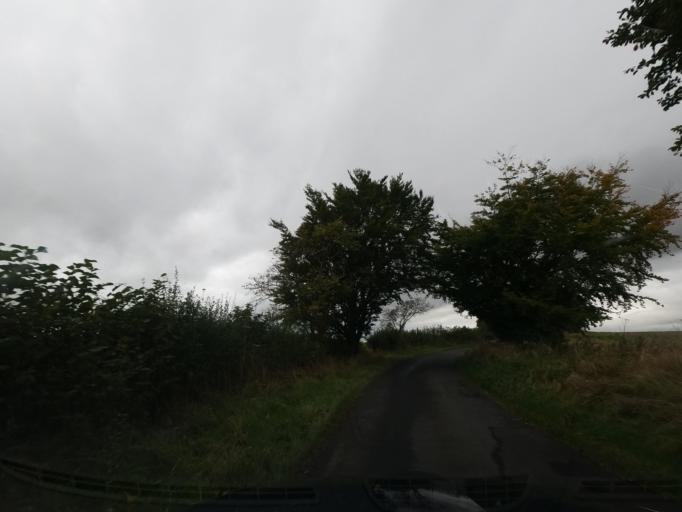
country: GB
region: England
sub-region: Northumberland
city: Ford
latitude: 55.6201
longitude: -2.0802
